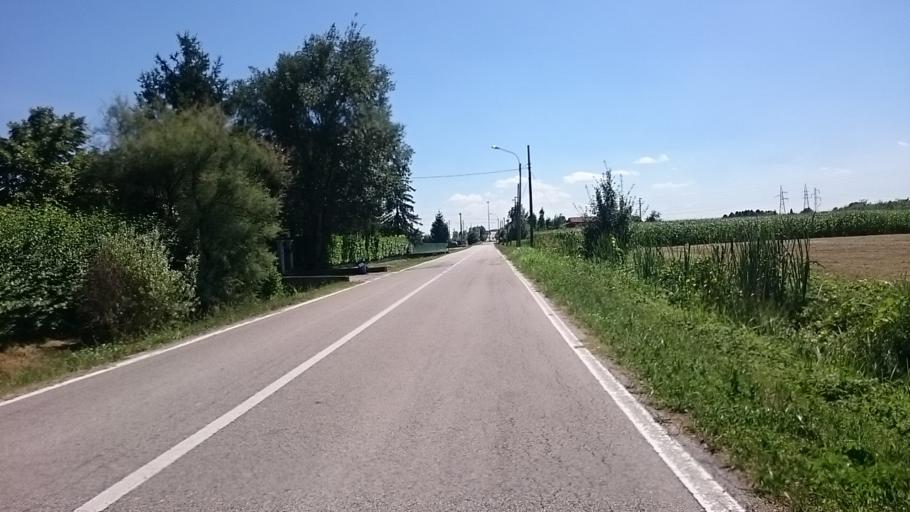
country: IT
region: Veneto
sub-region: Provincia di Venezia
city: Pianiga
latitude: 45.4509
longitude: 12.0286
